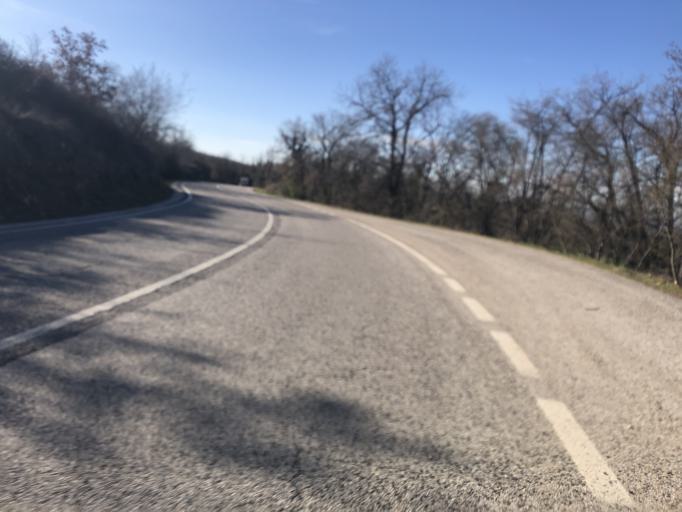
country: IT
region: Veneto
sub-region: Provincia di Verona
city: Volargne
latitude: 45.5419
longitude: 10.8340
